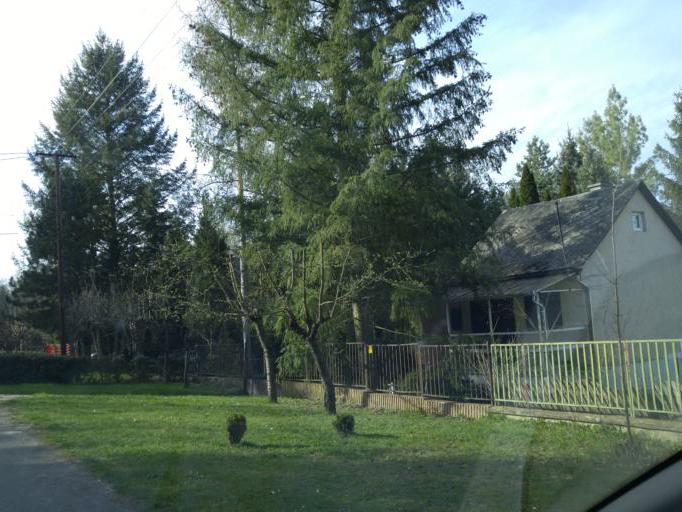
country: HU
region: Nograd
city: Retsag
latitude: 47.9196
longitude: 19.1763
